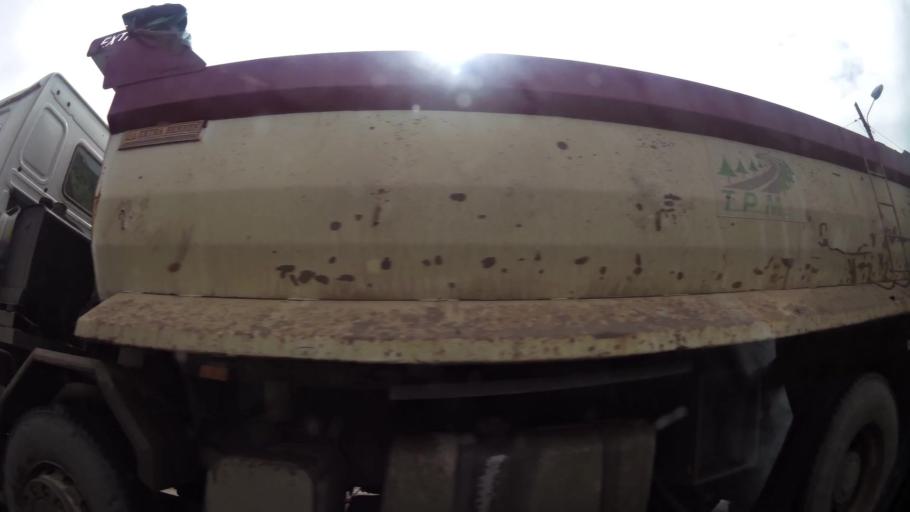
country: MA
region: Grand Casablanca
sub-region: Mediouna
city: Tit Mellil
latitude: 33.6402
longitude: -7.4755
